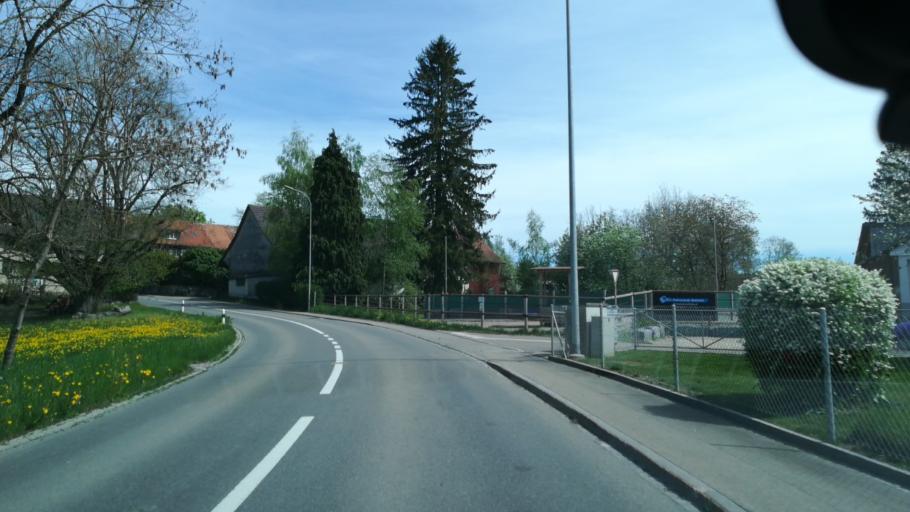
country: CH
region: Thurgau
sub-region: Weinfelden District
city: Maerstetten-Dorf
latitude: 47.6234
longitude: 9.0665
